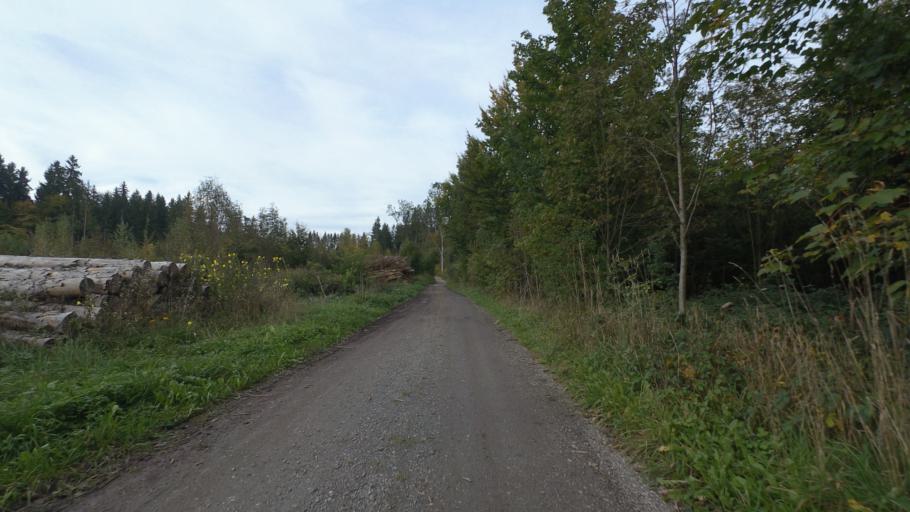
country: DE
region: Bavaria
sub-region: Upper Bavaria
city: Chieming
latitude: 47.9151
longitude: 12.5422
